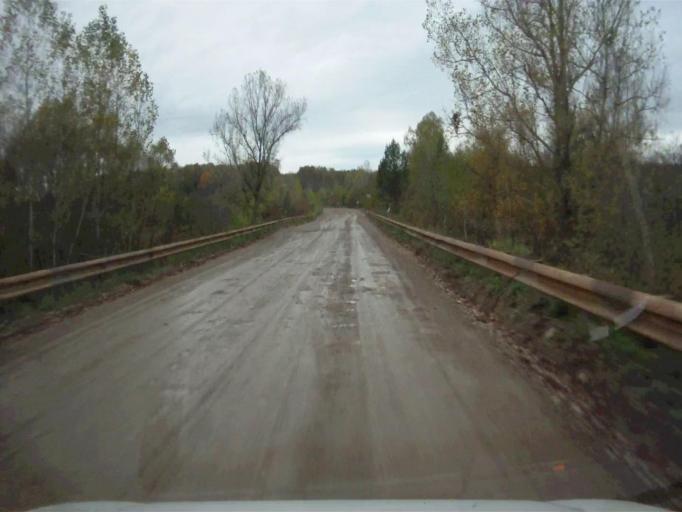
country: RU
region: Chelyabinsk
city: Nyazepetrovsk
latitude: 56.1323
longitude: 59.3187
